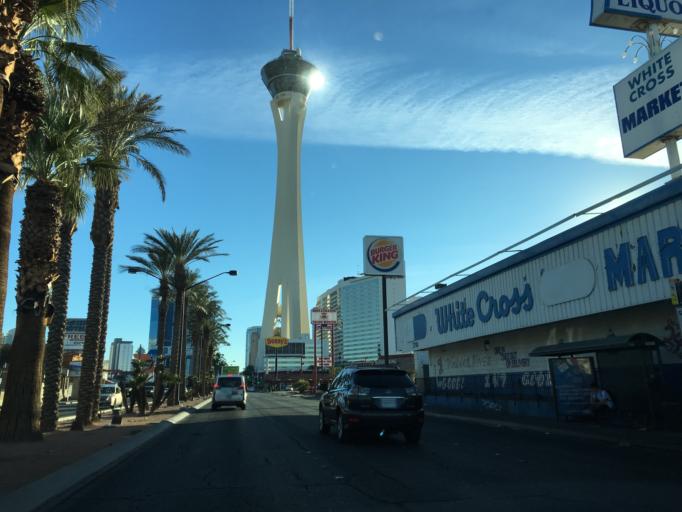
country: US
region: Nevada
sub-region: Clark County
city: Las Vegas
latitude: 36.1509
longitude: -115.1528
